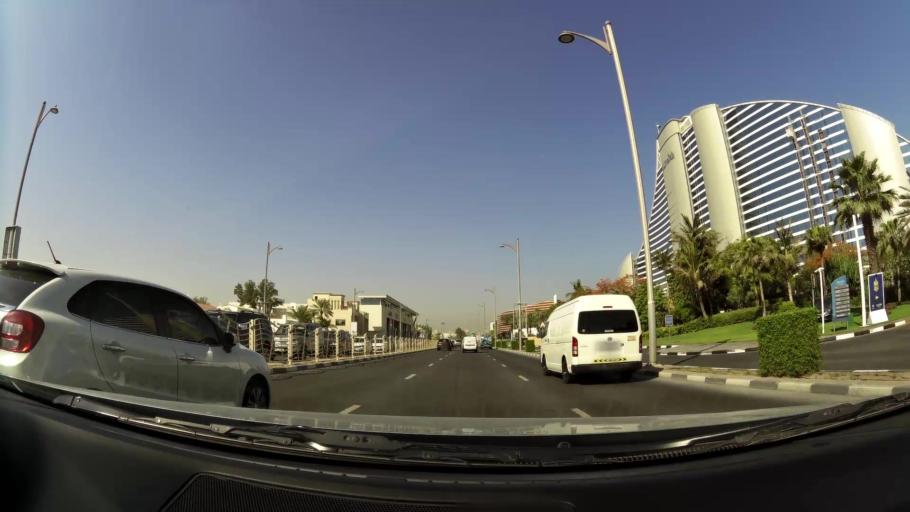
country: AE
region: Dubai
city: Dubai
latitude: 25.1423
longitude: 55.1924
